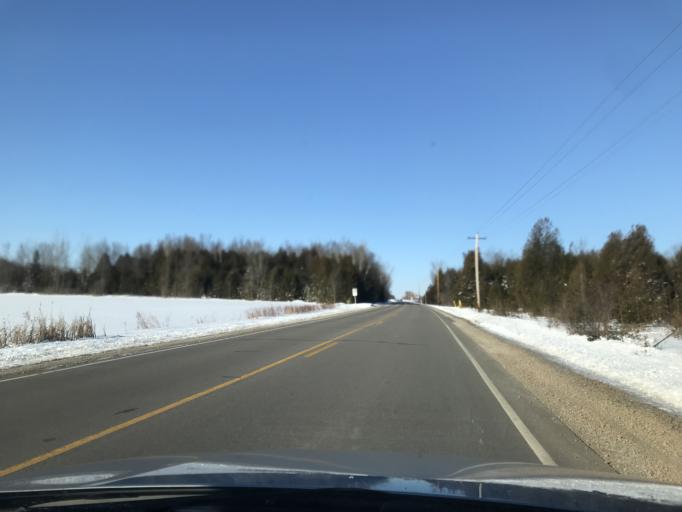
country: US
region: Wisconsin
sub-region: Oconto County
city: Oconto
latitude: 44.9505
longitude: -87.9885
